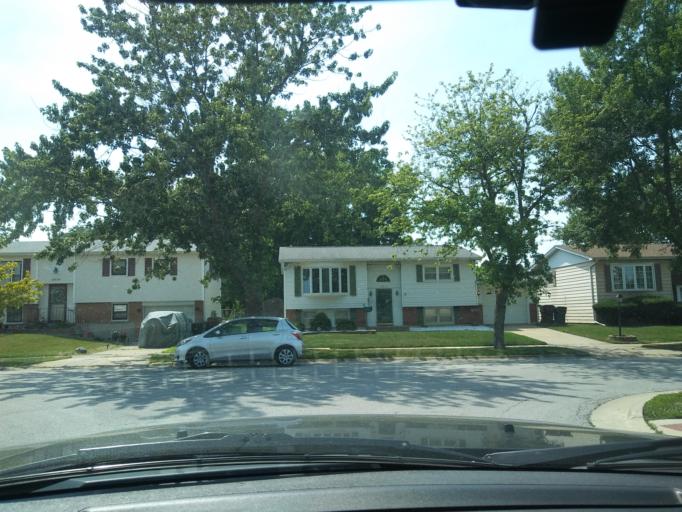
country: US
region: Illinois
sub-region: Cook County
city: Oak Forest
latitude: 41.6094
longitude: -87.7653
